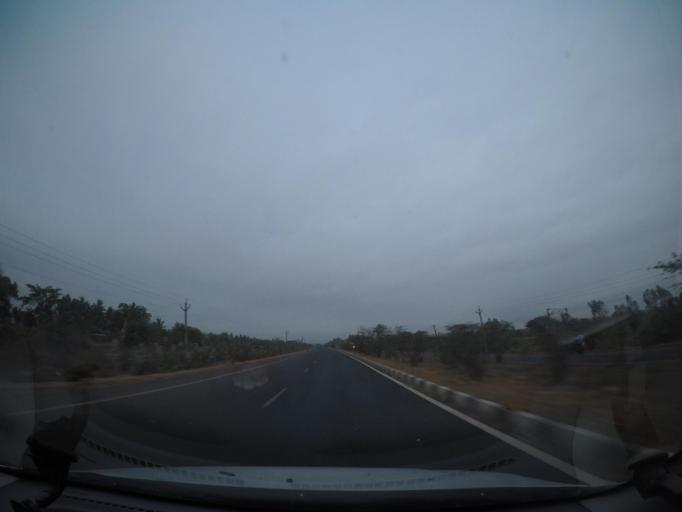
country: IN
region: Andhra Pradesh
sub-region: West Godavari
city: Tadepallegudem
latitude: 16.8087
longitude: 81.3195
